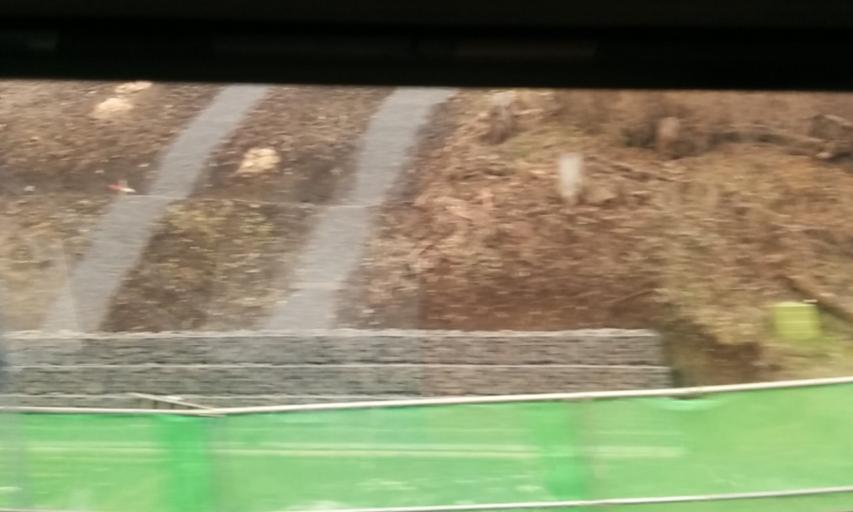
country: JP
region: Nagano
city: Ina
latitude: 35.9345
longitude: 137.7852
